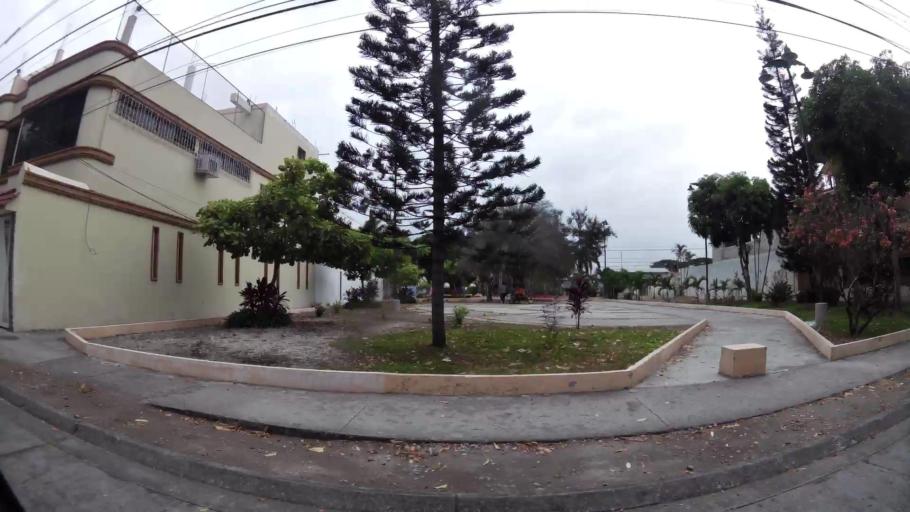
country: EC
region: Guayas
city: Eloy Alfaro
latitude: -2.1438
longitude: -79.8899
